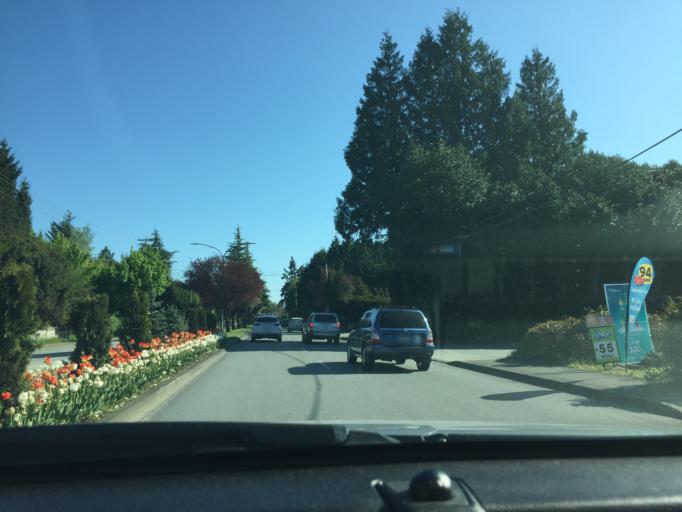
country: CA
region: British Columbia
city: Richmond
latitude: 49.1701
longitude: -123.1589
